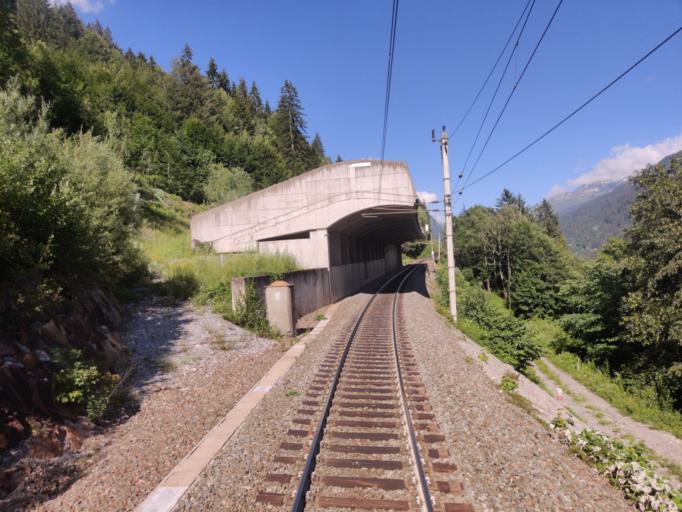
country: AT
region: Vorarlberg
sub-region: Politischer Bezirk Bludenz
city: Dalaas
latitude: 47.1286
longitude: 10.0136
